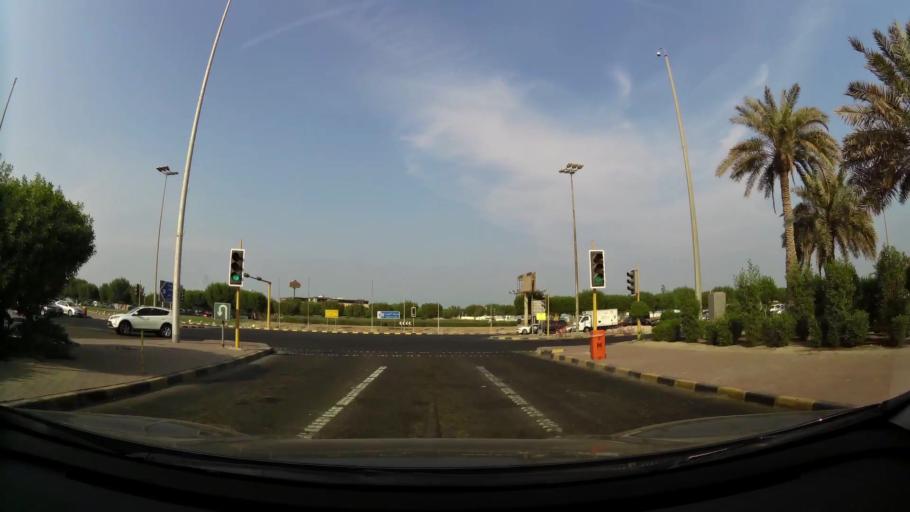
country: KW
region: Al Asimah
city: Ad Dasmah
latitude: 29.3685
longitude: 48.0128
